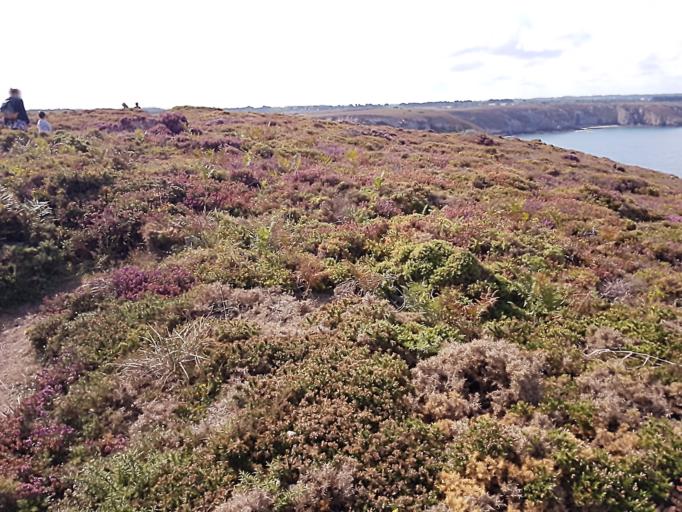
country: FR
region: Brittany
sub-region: Departement des Cotes-d'Armor
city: Saint-Cast-le-Guildo
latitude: 48.6818
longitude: -2.3268
